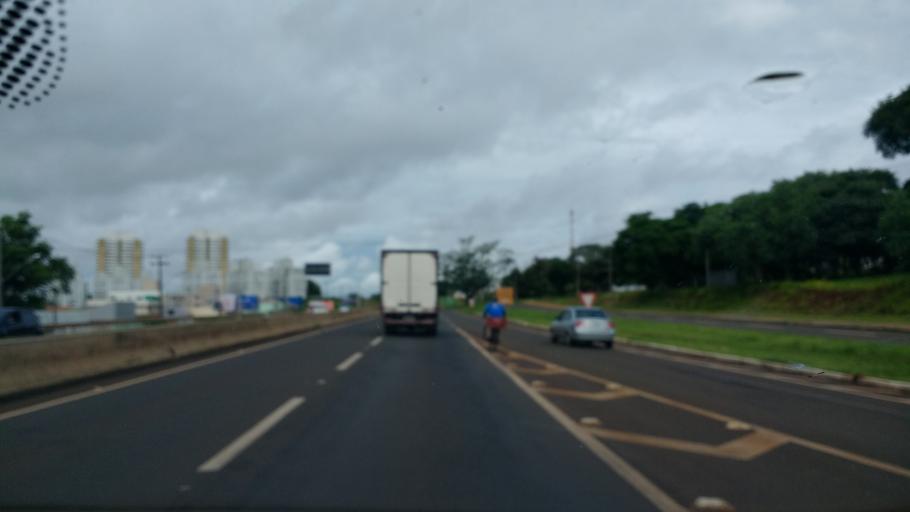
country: BR
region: Parana
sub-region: Londrina
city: Londrina
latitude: -23.3226
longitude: -51.1984
